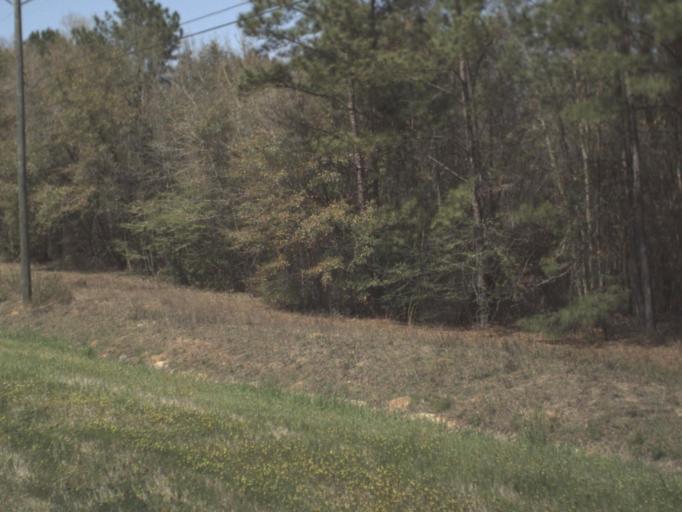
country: US
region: Florida
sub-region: Gadsden County
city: Quincy
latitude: 30.5609
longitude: -84.5371
